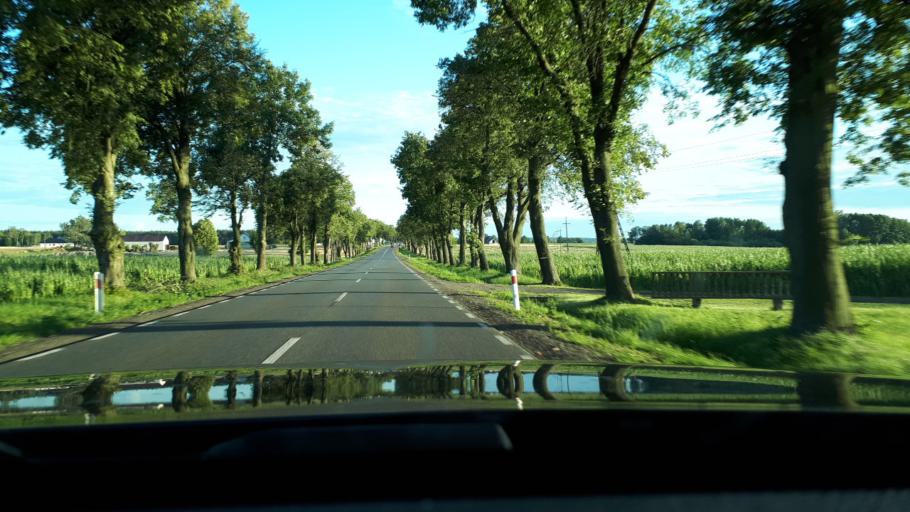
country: PL
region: Masovian Voivodeship
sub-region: Powiat ciechanowski
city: Ciechanow
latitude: 52.8243
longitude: 20.6159
